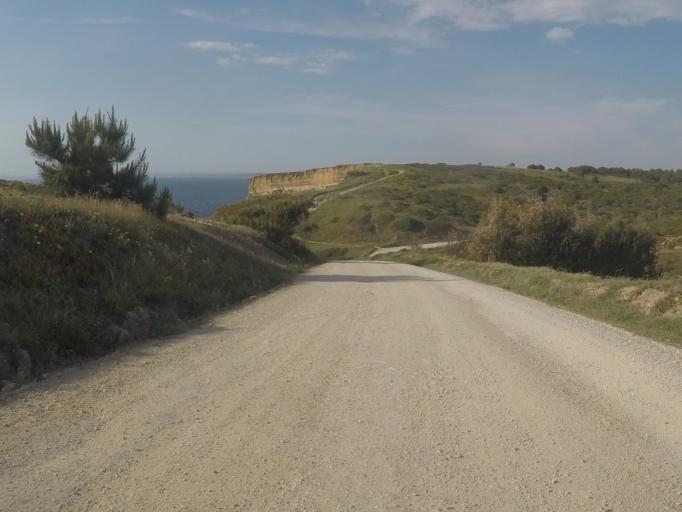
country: PT
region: Setubal
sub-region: Sesimbra
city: Sesimbra
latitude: 38.4508
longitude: -9.1988
